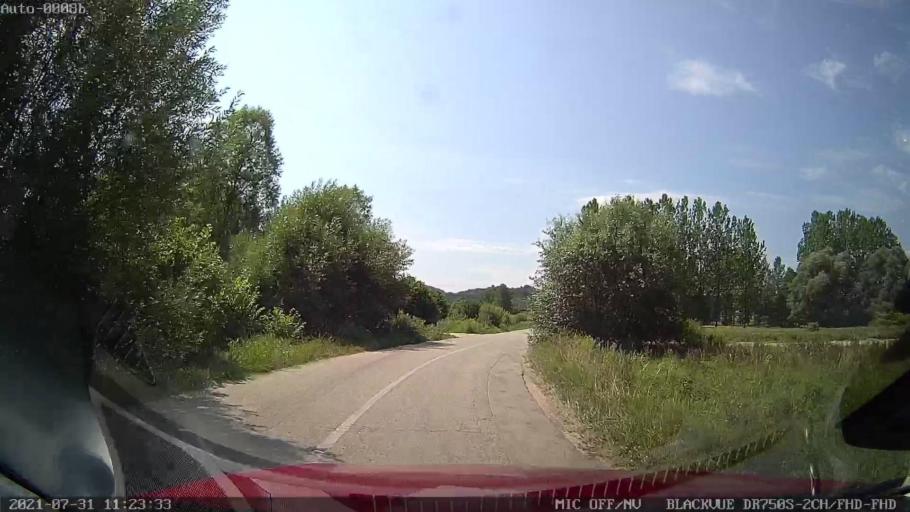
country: HR
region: Varazdinska
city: Jalzabet
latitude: 46.2156
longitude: 16.4619
